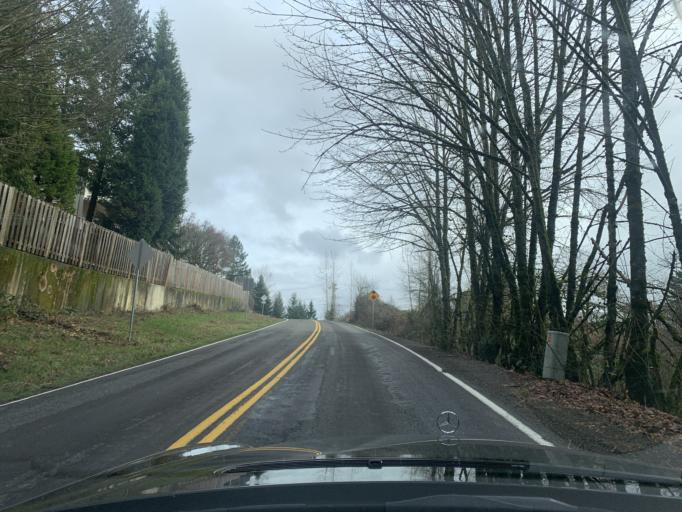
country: US
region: Oregon
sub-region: Multnomah County
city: Gresham
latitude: 45.4701
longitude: -122.4359
